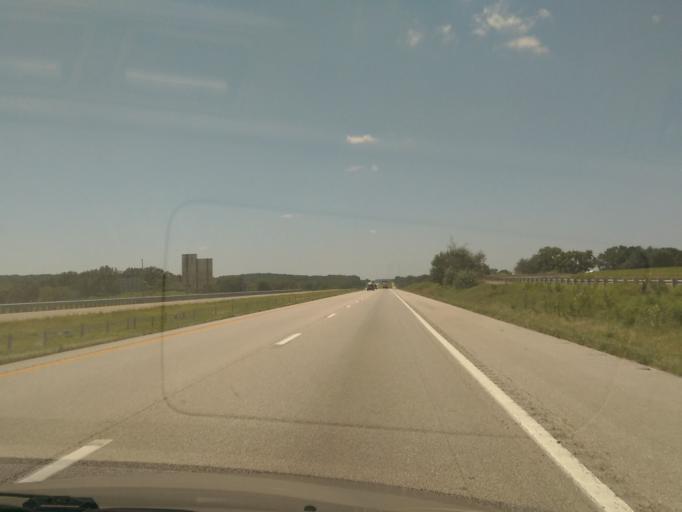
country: US
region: Missouri
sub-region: Cooper County
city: Boonville
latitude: 38.9353
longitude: -92.8642
